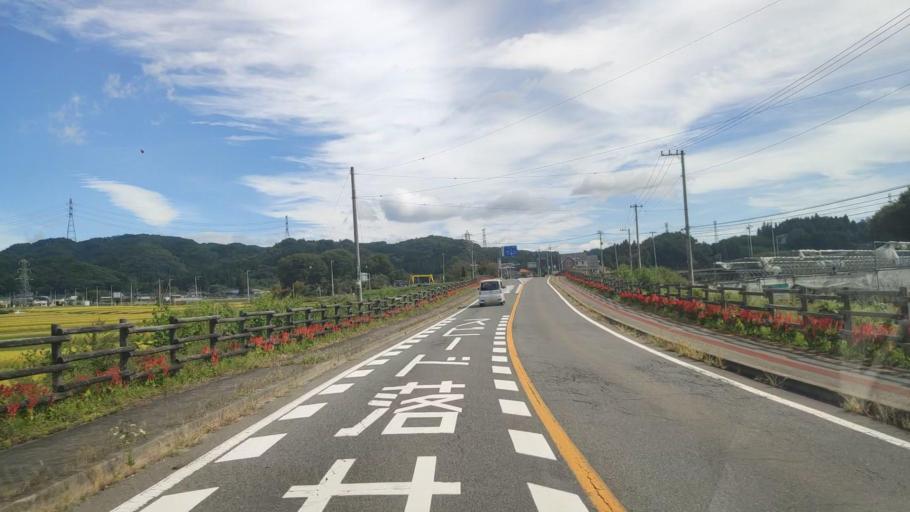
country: JP
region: Gunma
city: Numata
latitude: 36.6259
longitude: 138.9527
